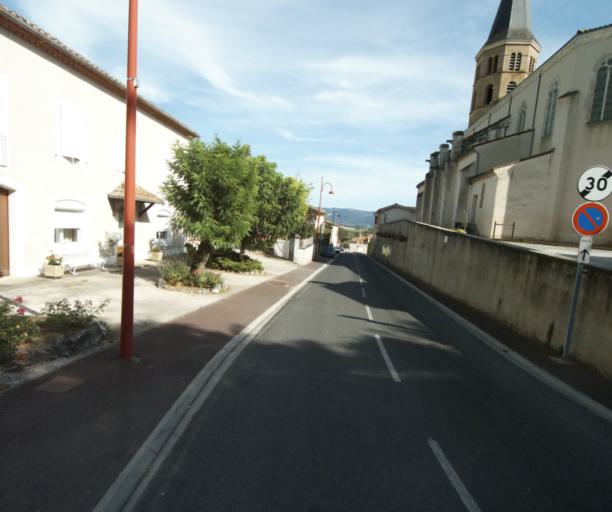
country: FR
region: Midi-Pyrenees
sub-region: Departement du Tarn
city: Soual
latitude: 43.5287
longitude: 2.0645
